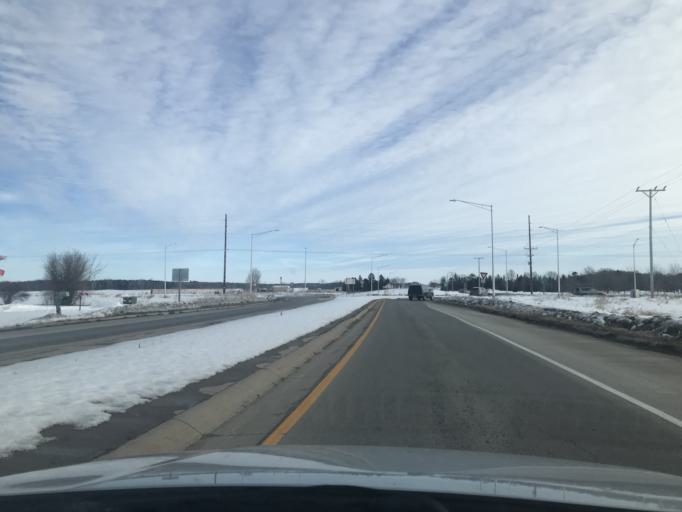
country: US
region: Wisconsin
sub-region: Oconto County
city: Gillett
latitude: 44.8961
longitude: -88.2481
